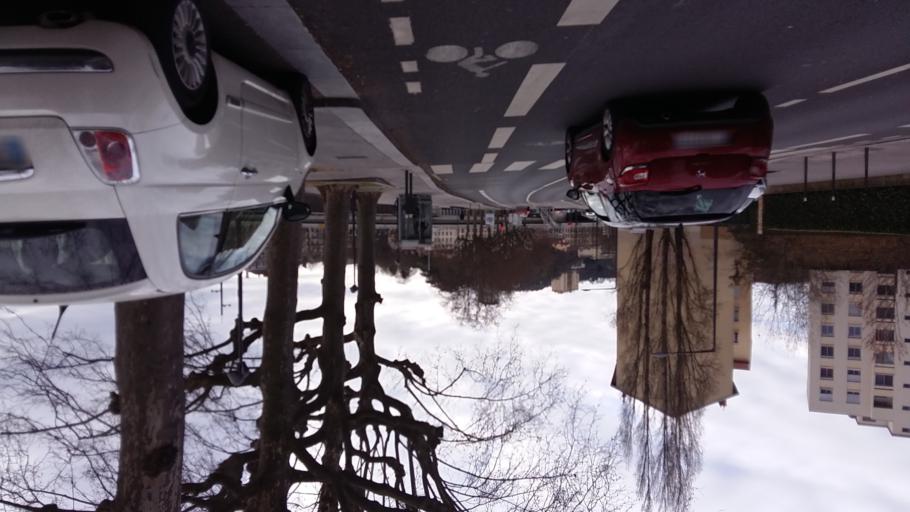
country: FR
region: Rhone-Alpes
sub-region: Departement du Rhone
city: Tassin-la-Demi-Lune
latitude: 45.7768
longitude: 4.8103
